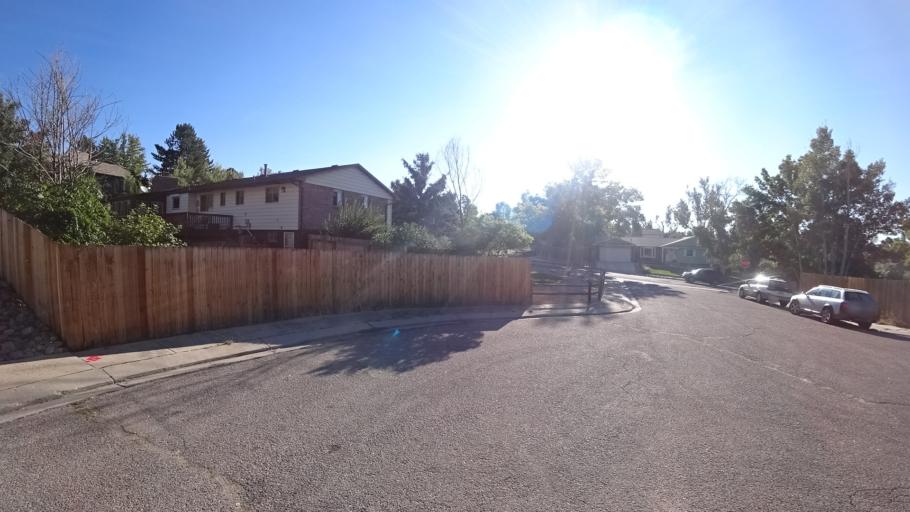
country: US
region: Colorado
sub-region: El Paso County
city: Cimarron Hills
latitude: 38.9111
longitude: -104.7558
